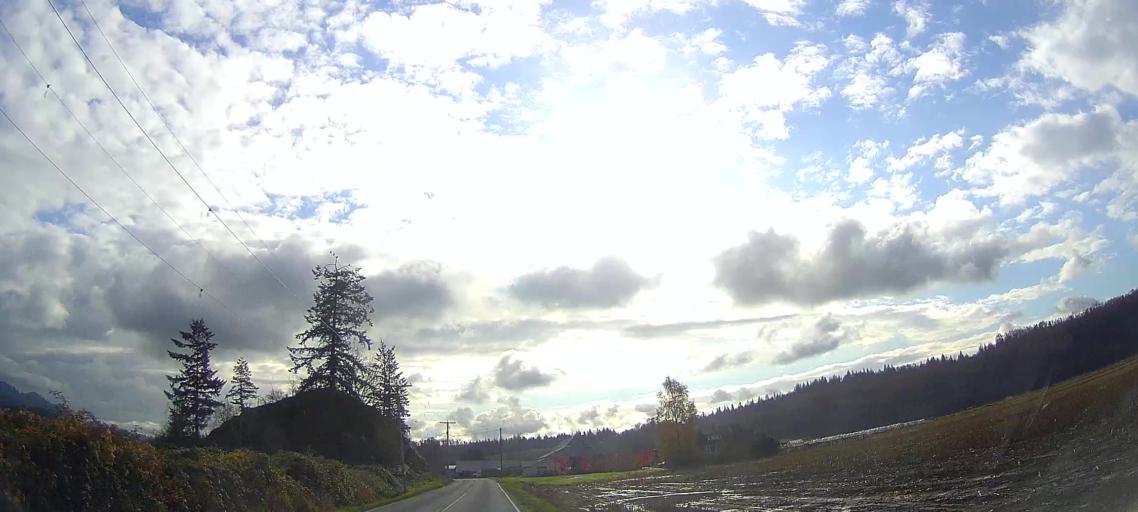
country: US
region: Washington
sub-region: Skagit County
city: Clear Lake
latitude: 48.4350
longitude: -122.2210
